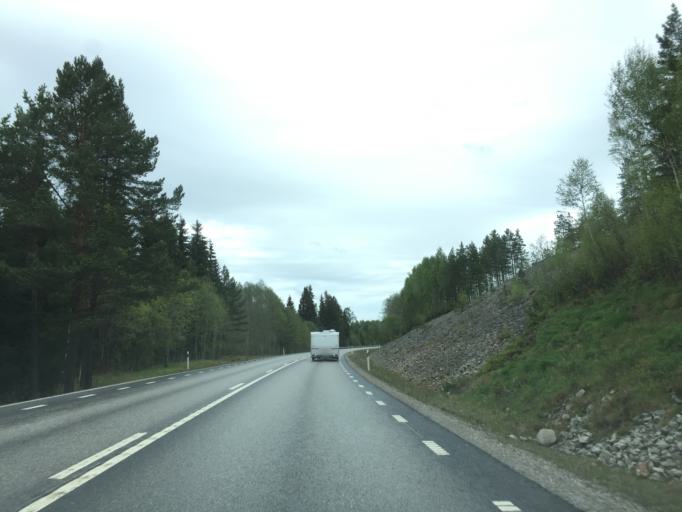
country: SE
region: OErebro
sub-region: Lindesbergs Kommun
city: Lindesberg
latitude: 59.6075
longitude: 15.1843
